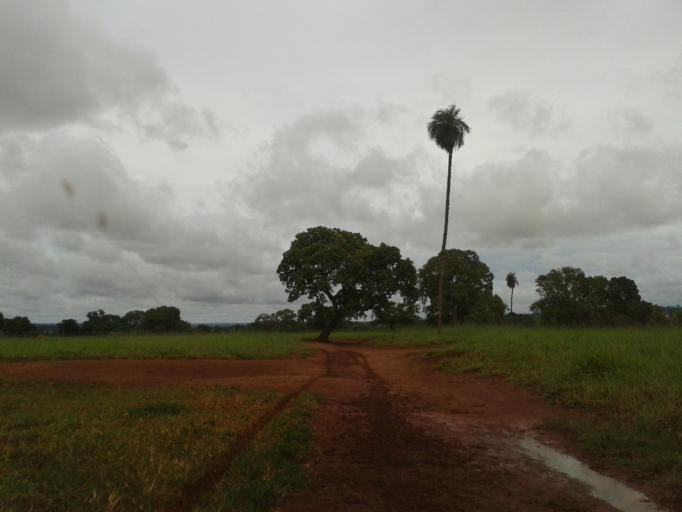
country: BR
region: Minas Gerais
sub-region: Capinopolis
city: Capinopolis
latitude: -18.7796
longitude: -49.7720
